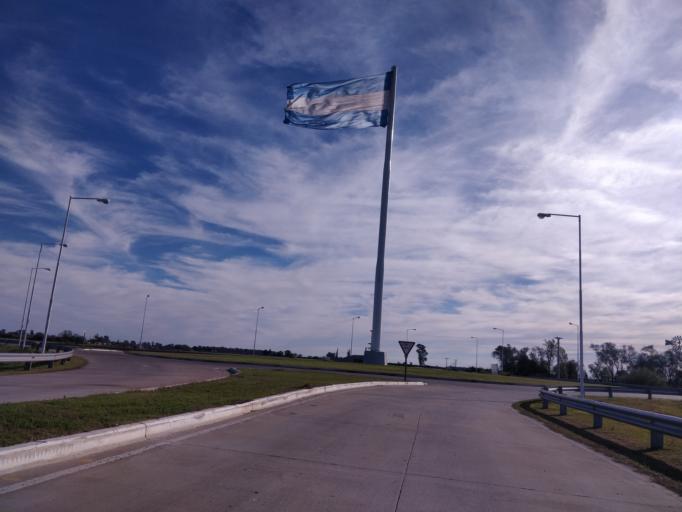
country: AR
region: Cordoba
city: Leones
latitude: -32.6423
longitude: -62.2896
